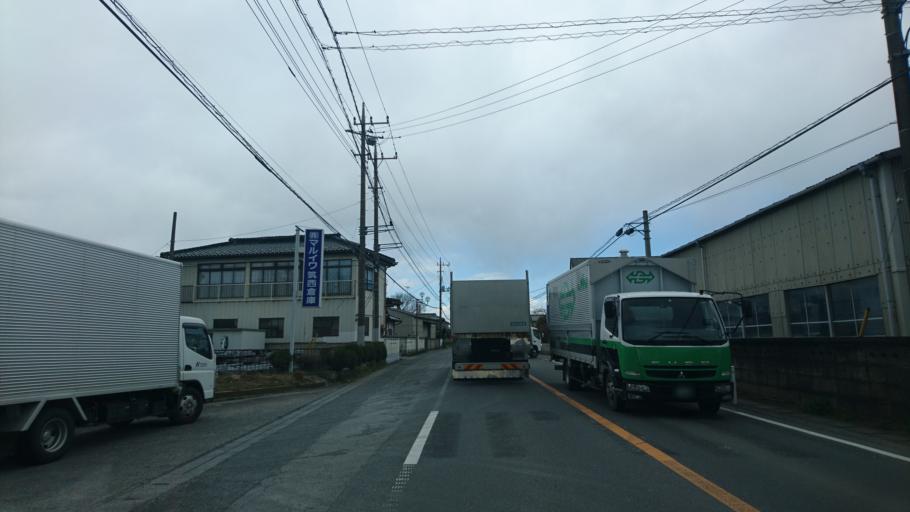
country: JP
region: Ibaraki
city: Yuki
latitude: 36.2842
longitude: 139.9138
